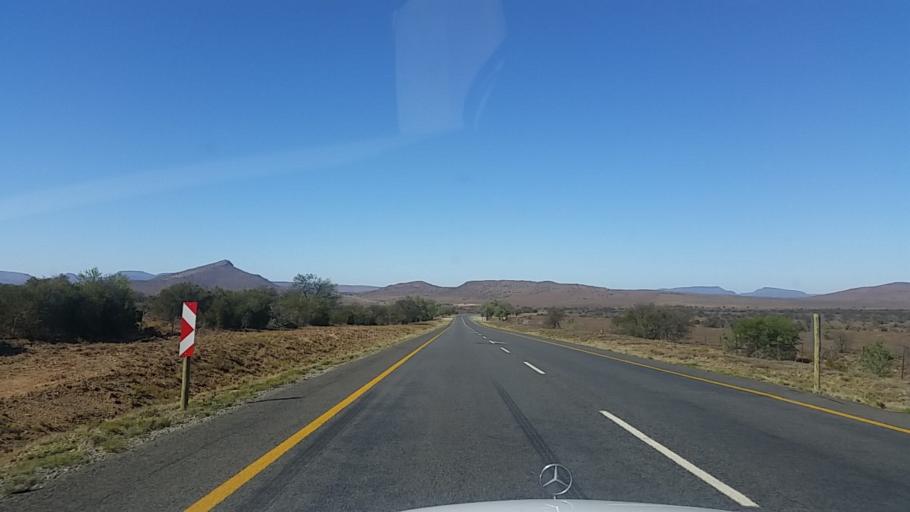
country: ZA
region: Eastern Cape
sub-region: Cacadu District Municipality
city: Graaff-Reinet
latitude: -32.0659
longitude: 24.6062
